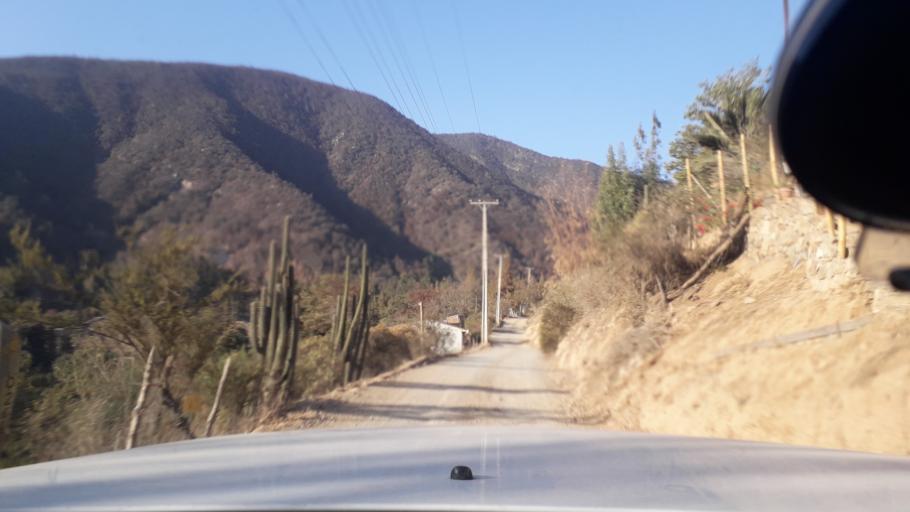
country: CL
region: Valparaiso
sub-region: Provincia de Marga Marga
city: Limache
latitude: -33.0530
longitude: -71.0892
